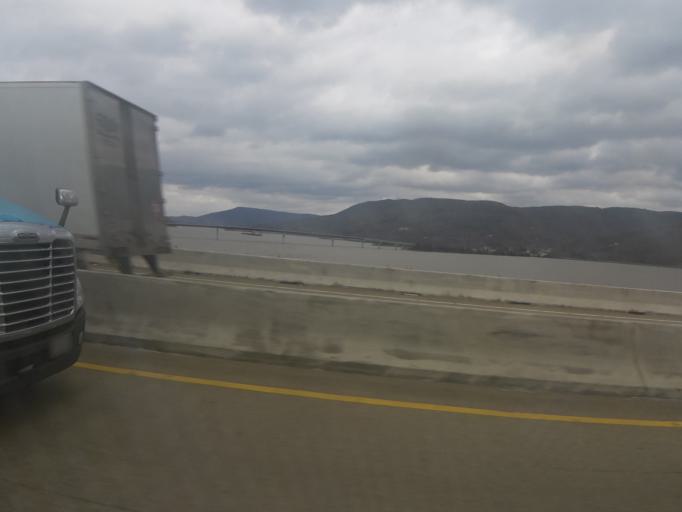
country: US
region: Tennessee
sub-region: Marion County
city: Jasper
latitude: 35.0210
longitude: -85.5499
